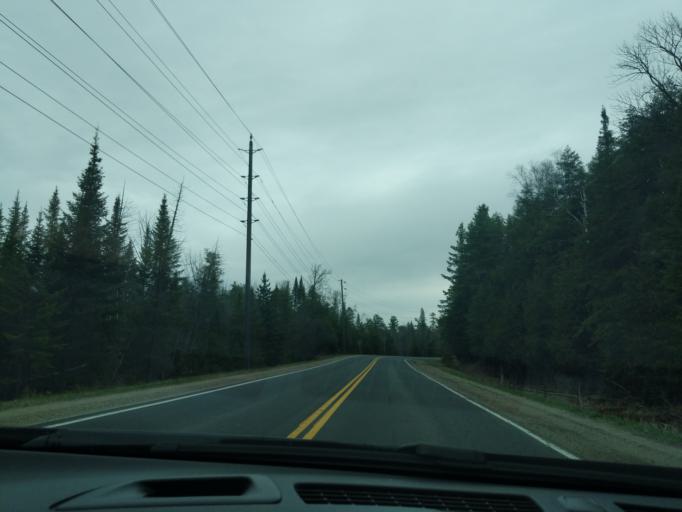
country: CA
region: Ontario
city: Orangeville
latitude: 44.0143
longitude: -79.9829
